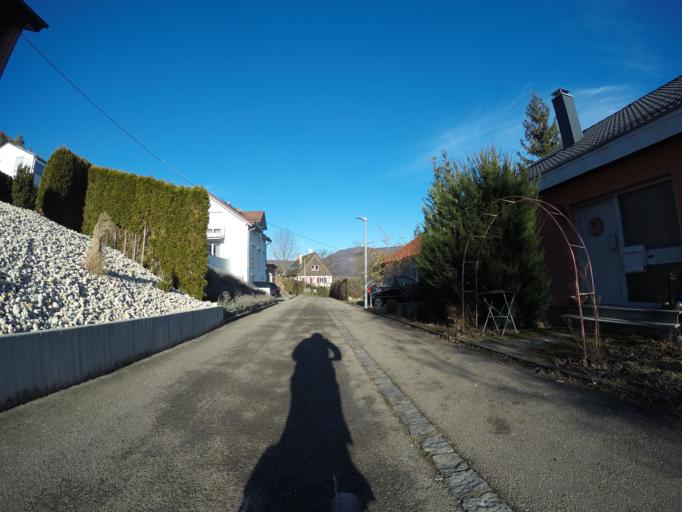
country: DE
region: Baden-Wuerttemberg
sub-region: Tuebingen Region
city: Pfullingen
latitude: 48.4307
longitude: 9.2533
